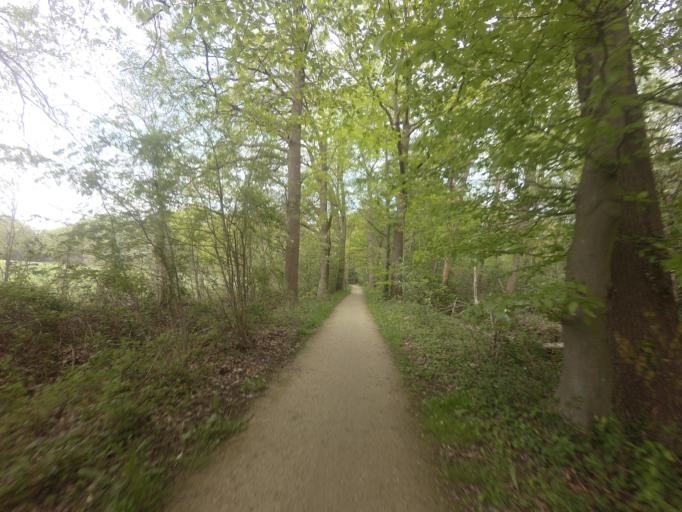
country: NL
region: Overijssel
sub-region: Gemeente Hof van Twente
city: Delden
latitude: 52.2196
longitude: 6.7335
